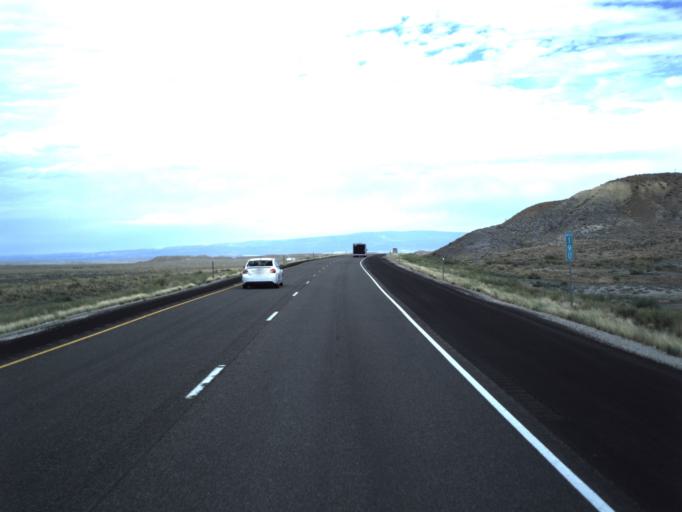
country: US
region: Utah
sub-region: Grand County
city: Moab
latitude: 38.9497
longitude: -109.6788
